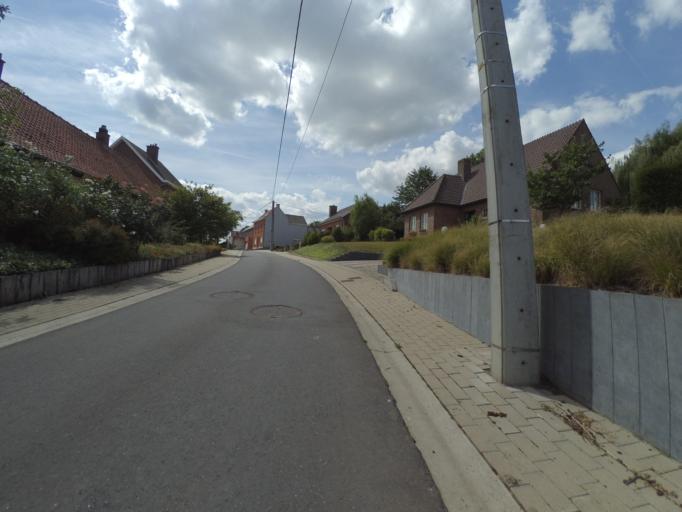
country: BE
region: Flanders
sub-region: Provincie Oost-Vlaanderen
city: Zottegem
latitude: 50.8462
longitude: 3.7470
